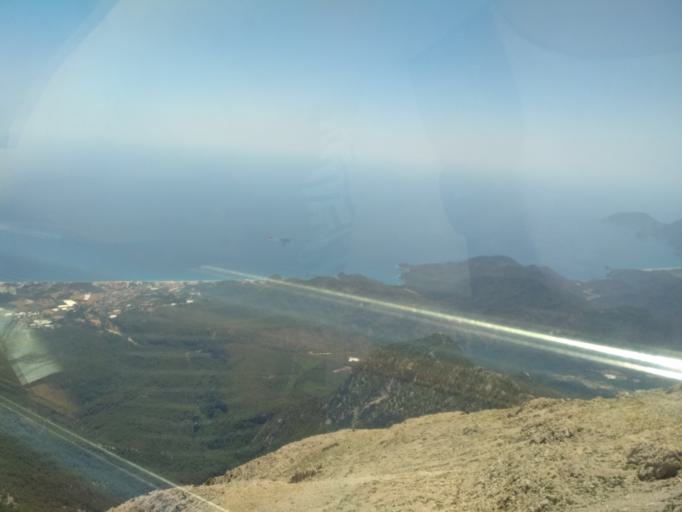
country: TR
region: Antalya
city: Tekirova
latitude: 36.5364
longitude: 30.4447
